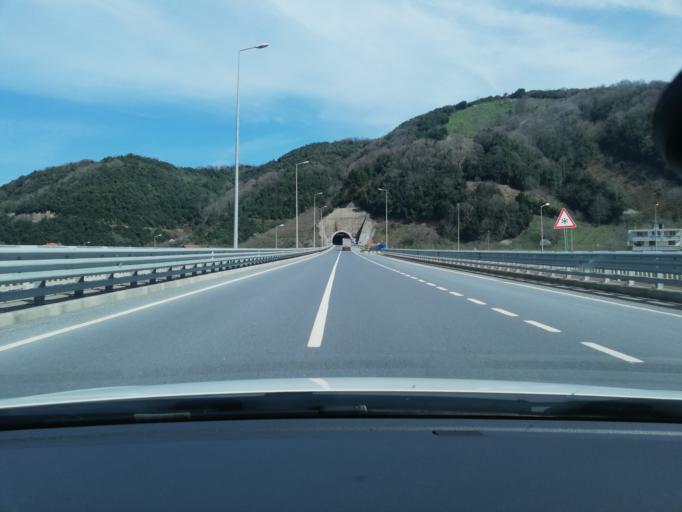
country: TR
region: Zonguldak
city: Alapli
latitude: 41.1517
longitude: 31.3520
